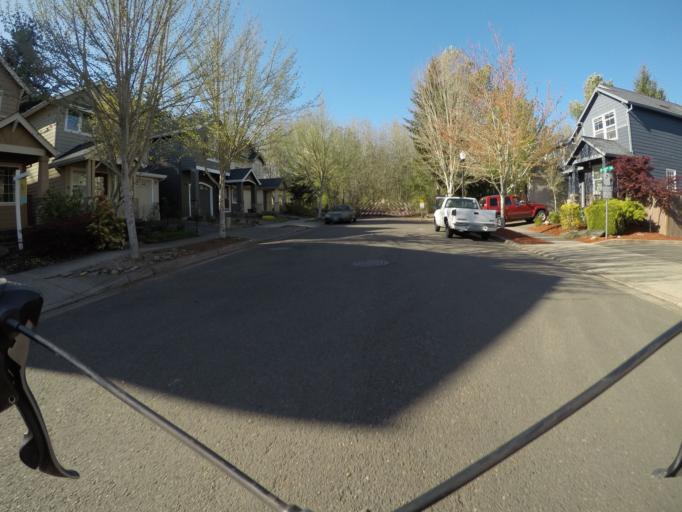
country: US
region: Oregon
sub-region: Washington County
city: King City
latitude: 45.3997
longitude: -122.8148
